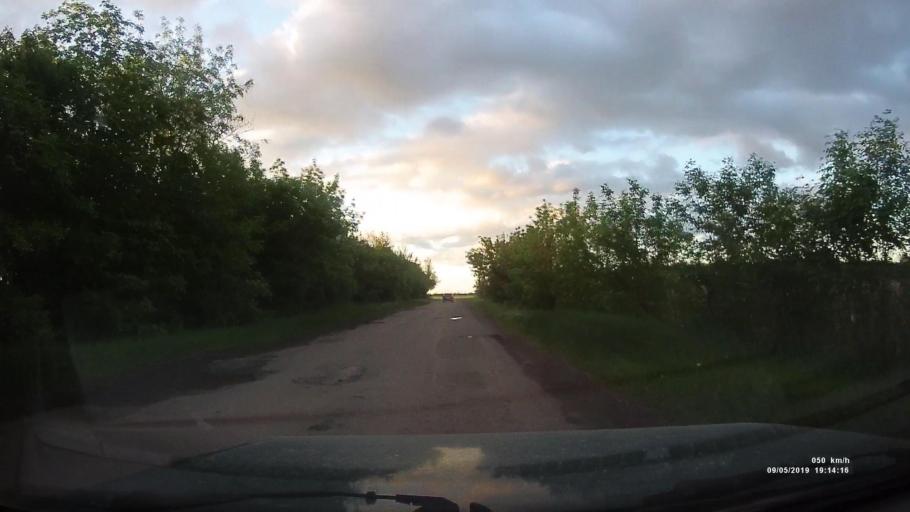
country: RU
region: Krasnodarskiy
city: Kanelovskaya
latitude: 46.7568
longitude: 39.2140
